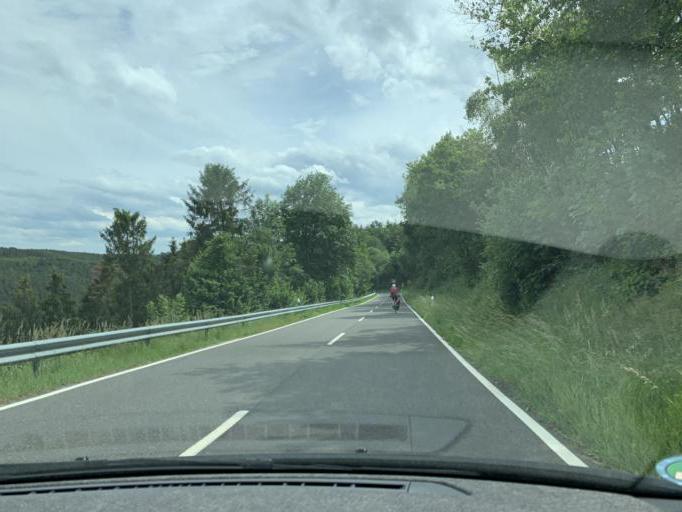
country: DE
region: North Rhine-Westphalia
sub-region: Regierungsbezirk Koln
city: Hurtgenwald
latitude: 50.6871
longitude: 6.3875
